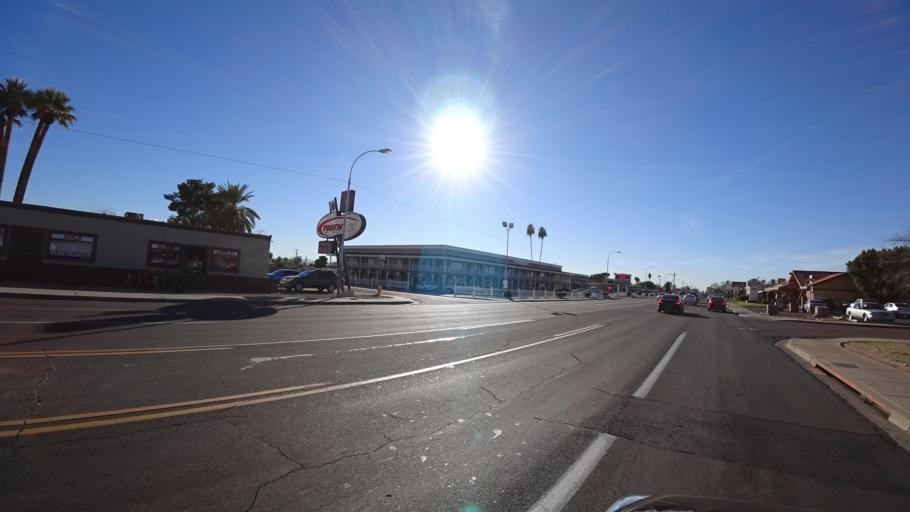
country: US
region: Arizona
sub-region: Maricopa County
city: Phoenix
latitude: 33.4805
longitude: -112.0061
